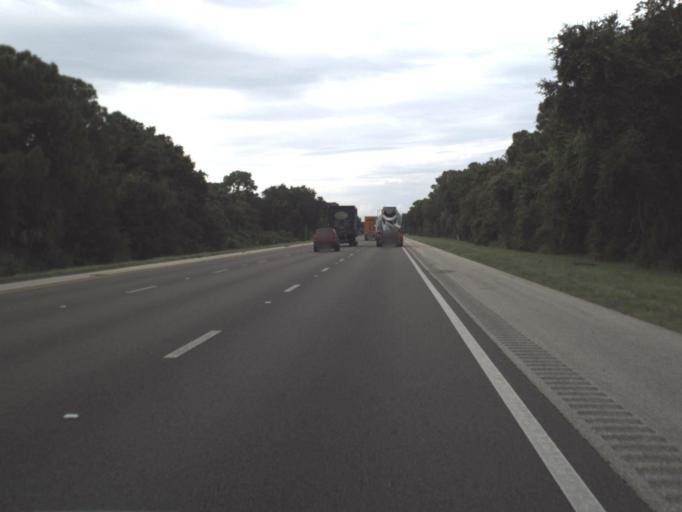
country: US
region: Florida
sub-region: Sarasota County
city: Bee Ridge
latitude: 27.2448
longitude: -82.4509
